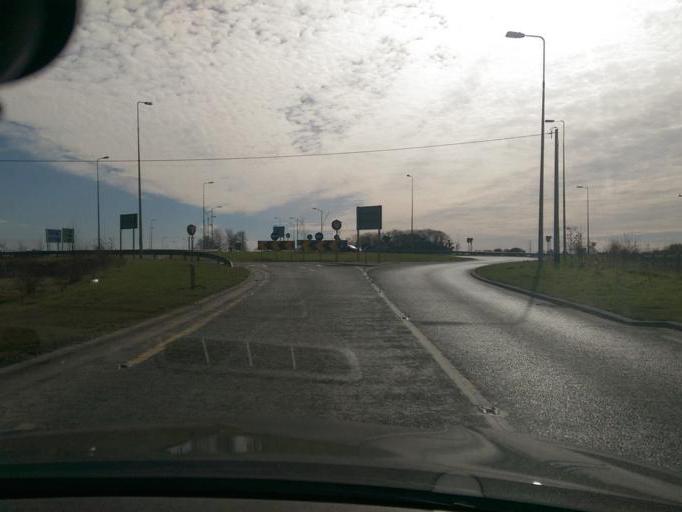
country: IE
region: Connaught
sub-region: County Galway
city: Oranmore
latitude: 53.2966
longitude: -8.9238
